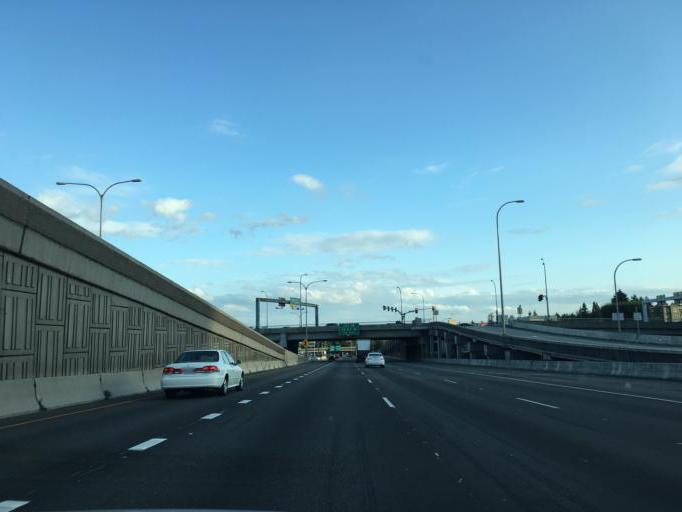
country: US
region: Washington
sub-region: King County
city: Bellevue
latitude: 47.6151
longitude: -122.1890
